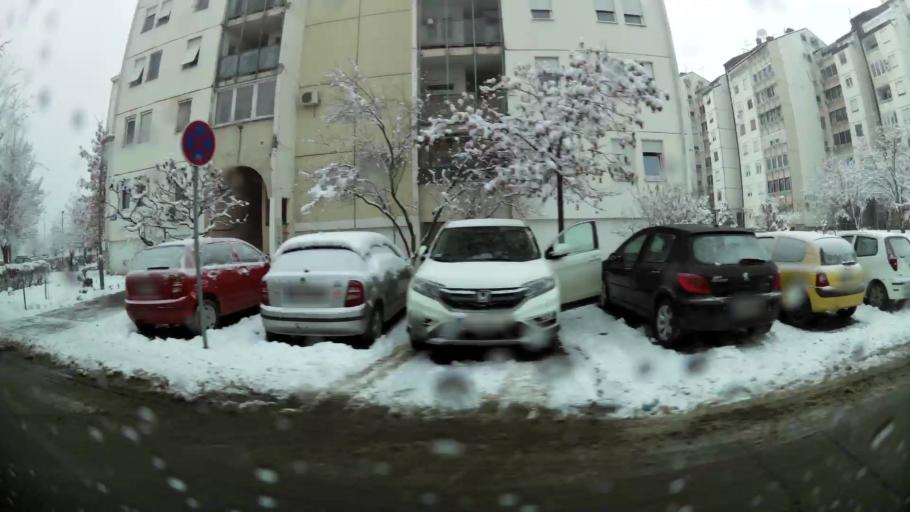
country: RS
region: Central Serbia
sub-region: Belgrade
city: Cukarica
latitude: 44.7938
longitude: 20.3737
